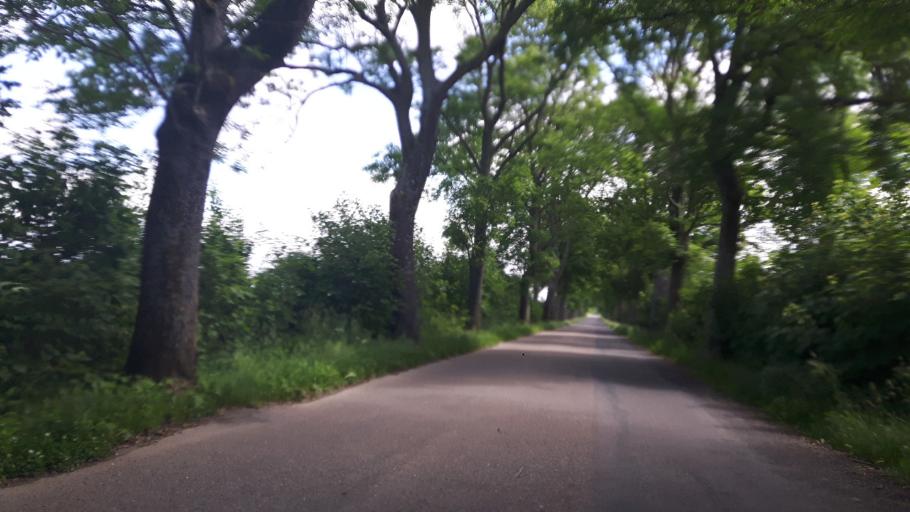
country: PL
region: West Pomeranian Voivodeship
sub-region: Powiat slawienski
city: Slawno
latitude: 54.5087
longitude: 16.5842
